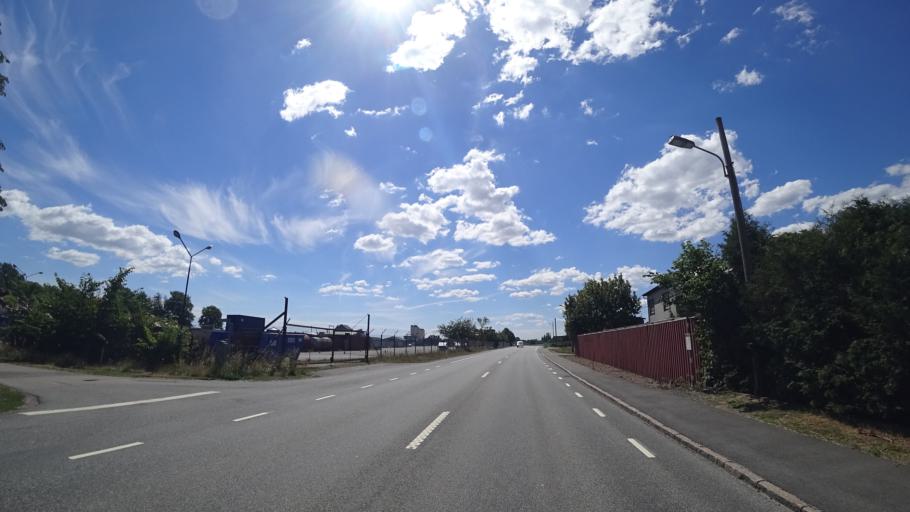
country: SE
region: Skane
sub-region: Kristianstads Kommun
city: Kristianstad
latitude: 56.0493
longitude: 14.0883
